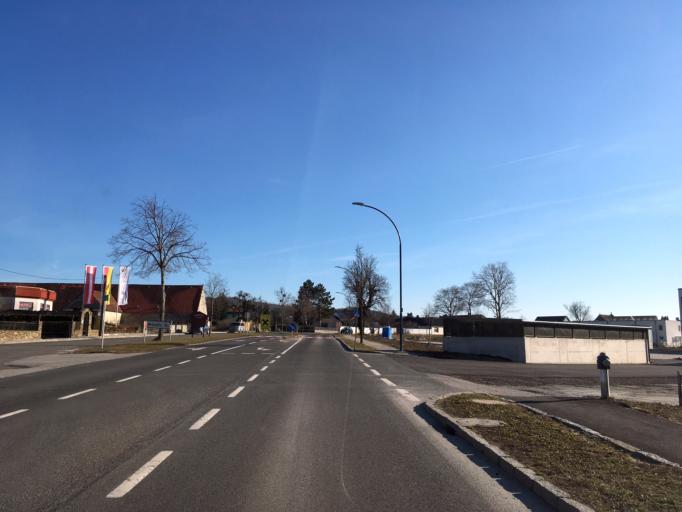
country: AT
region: Burgenland
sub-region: Eisenstadt-Umgebung
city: Hornstein
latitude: 47.8841
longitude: 16.4400
